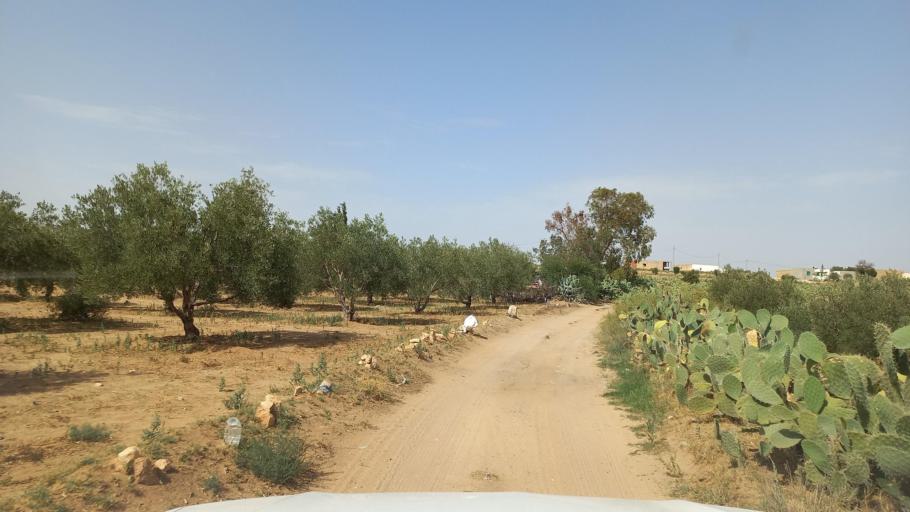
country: TN
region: Al Qasrayn
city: Kasserine
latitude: 35.2970
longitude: 8.9477
